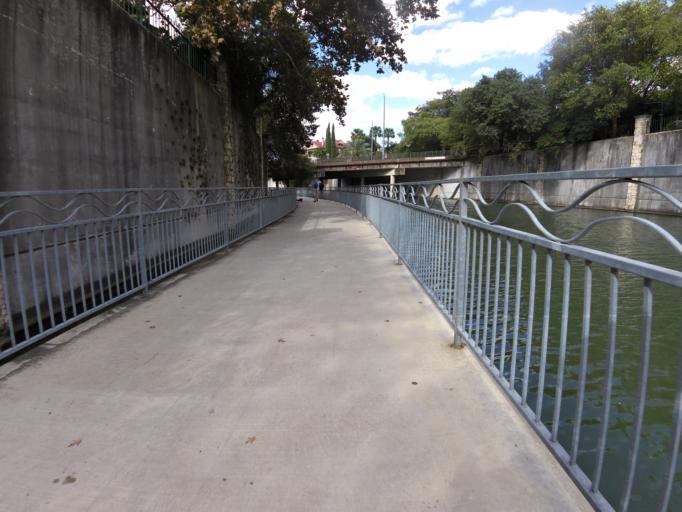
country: US
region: Texas
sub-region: Bexar County
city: San Antonio
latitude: 29.4112
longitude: -98.4956
